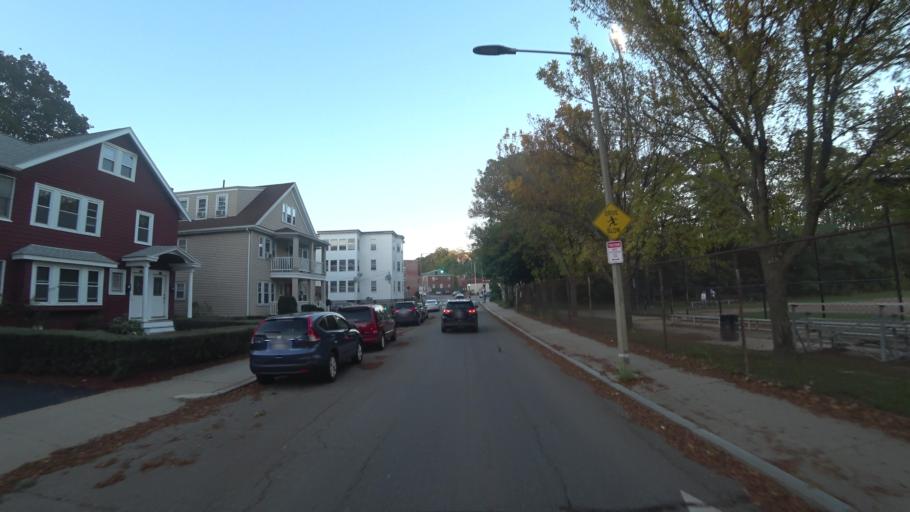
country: US
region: Massachusetts
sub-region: Middlesex County
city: Watertown
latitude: 42.3482
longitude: -71.1609
